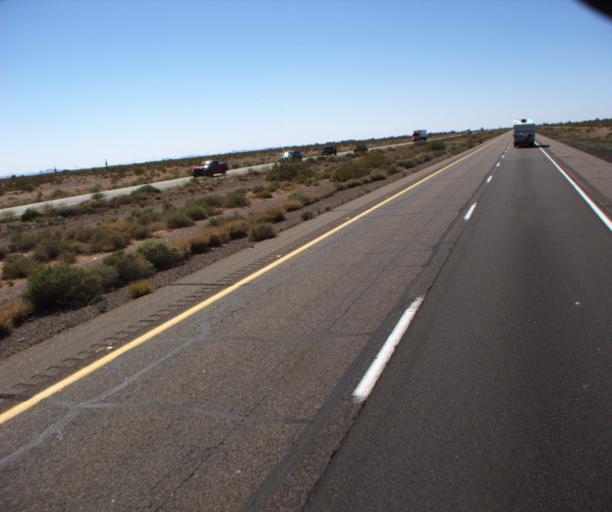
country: US
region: Arizona
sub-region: Maricopa County
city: Gila Bend
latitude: 32.9022
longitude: -113.0029
